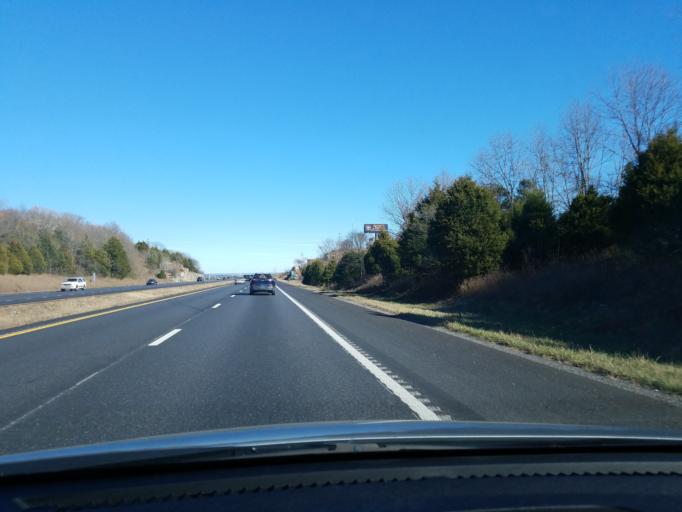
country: US
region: Missouri
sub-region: Taney County
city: Hollister
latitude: 36.5848
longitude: -93.2345
